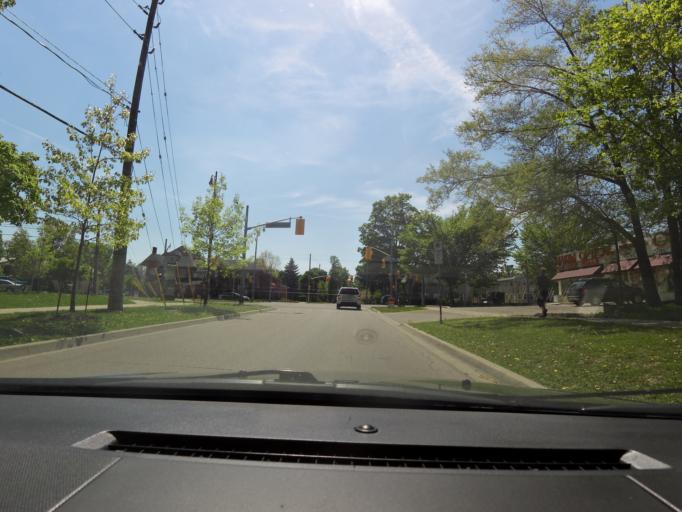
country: CA
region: Ontario
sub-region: Wellington County
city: Guelph
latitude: 43.5490
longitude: -80.2548
